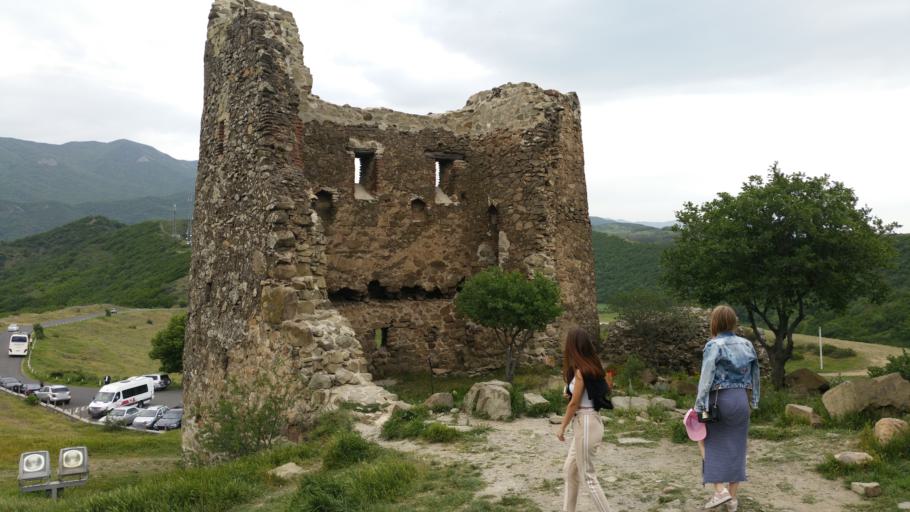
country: GE
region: Mtskheta-Mtianeti
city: Mtskheta
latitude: 41.8386
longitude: 44.7337
